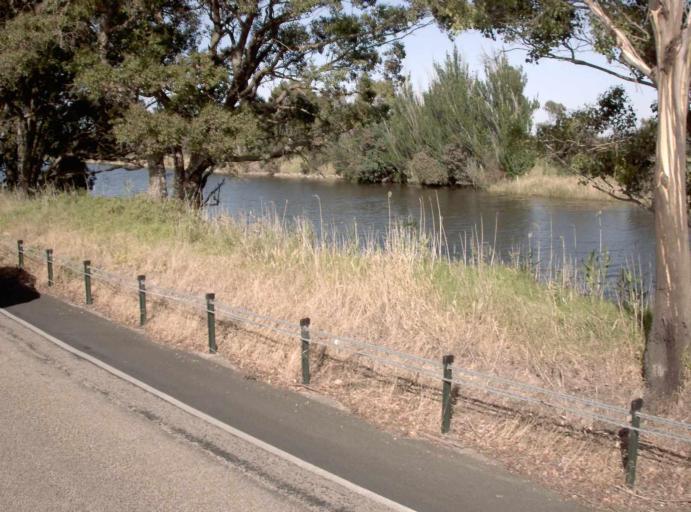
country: AU
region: Victoria
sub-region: East Gippsland
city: Lakes Entrance
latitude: -37.8407
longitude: 147.8592
